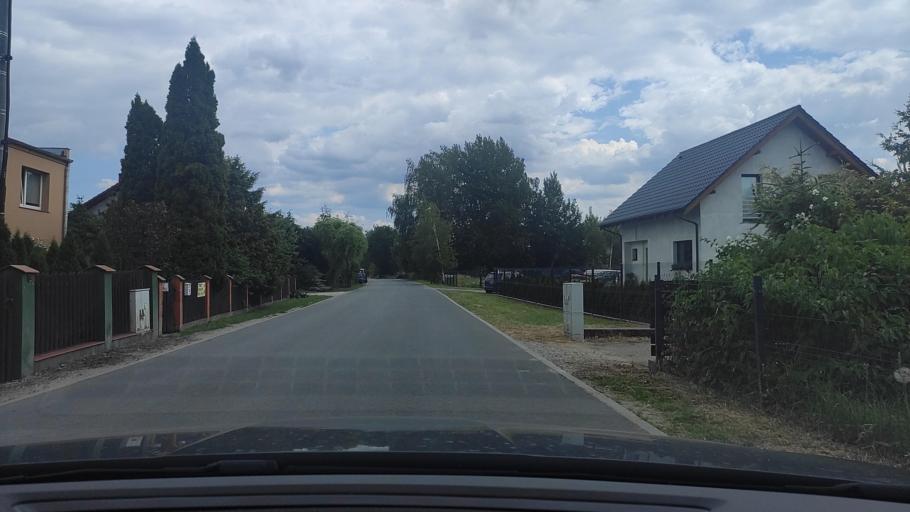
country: PL
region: Greater Poland Voivodeship
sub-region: Powiat poznanski
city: Pobiedziska
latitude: 52.4952
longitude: 17.1873
